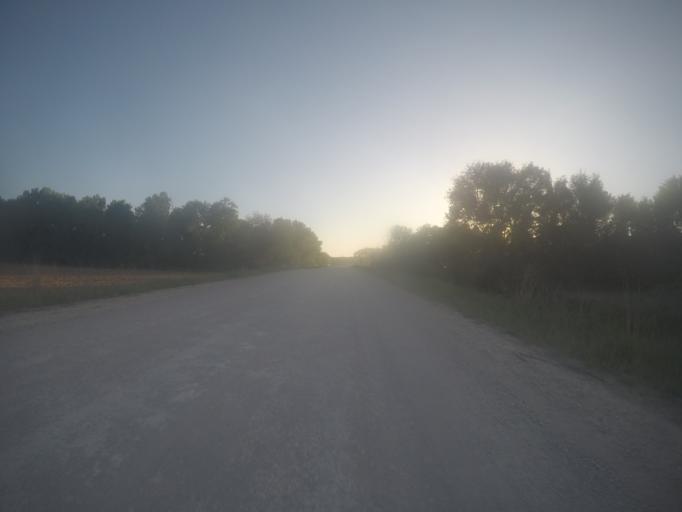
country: US
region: Kansas
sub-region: Riley County
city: Manhattan
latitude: 39.2422
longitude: -96.5658
